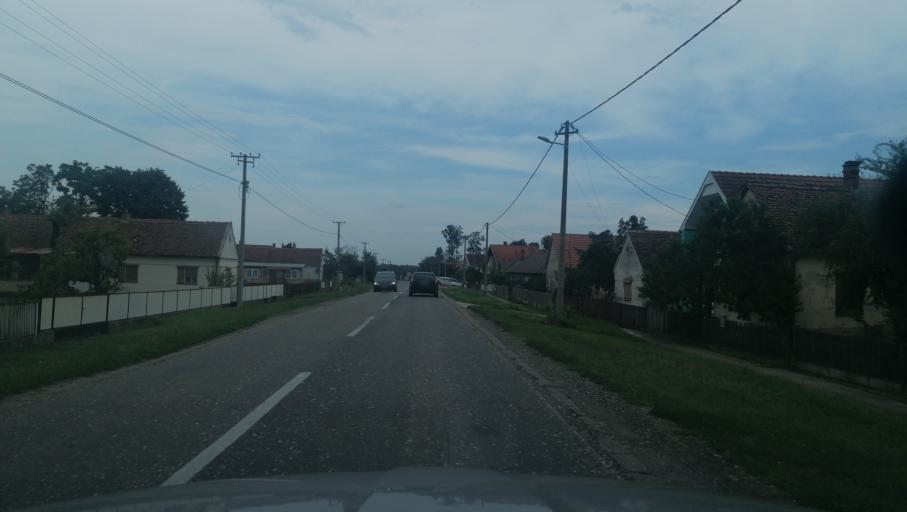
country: RS
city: Klenje
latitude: 44.8109
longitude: 19.4408
